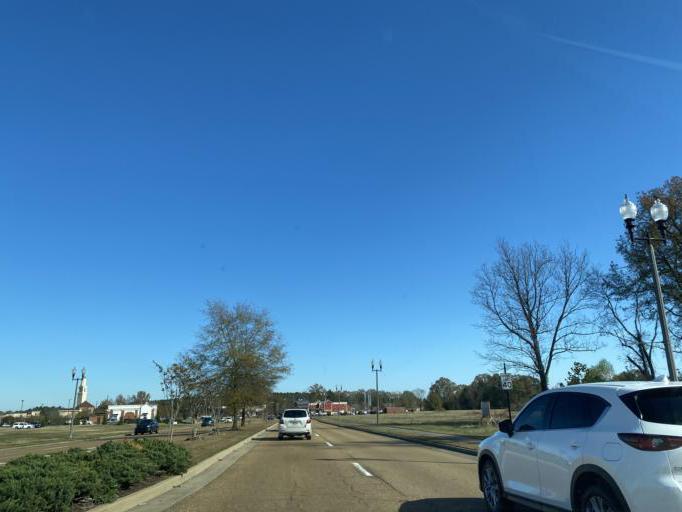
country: US
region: Mississippi
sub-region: Madison County
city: Madison
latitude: 32.4612
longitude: -90.1370
